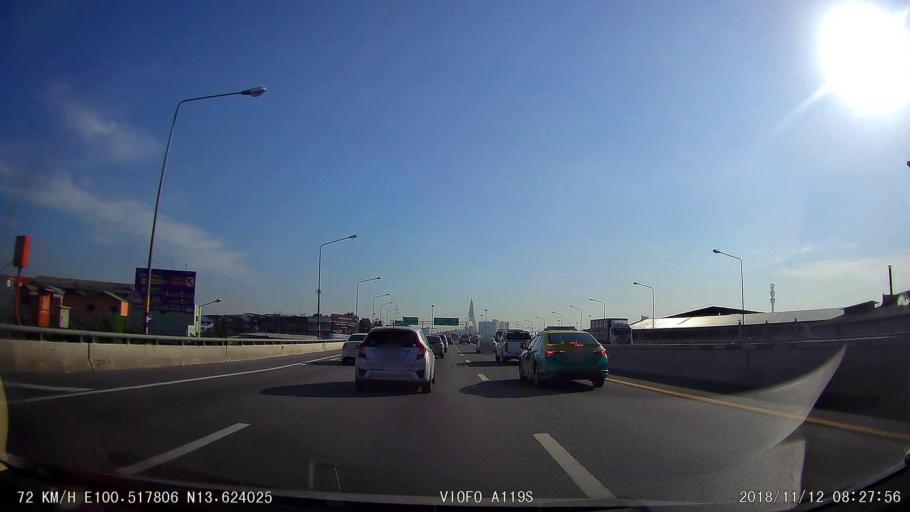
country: TH
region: Bangkok
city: Thung Khru
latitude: 13.6242
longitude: 100.5180
